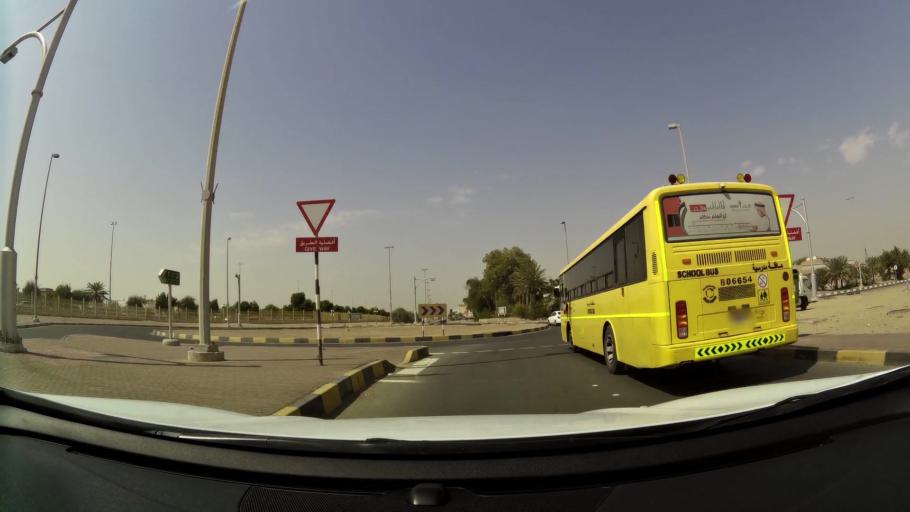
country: AE
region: Abu Dhabi
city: Abu Dhabi
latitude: 24.2889
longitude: 54.6387
